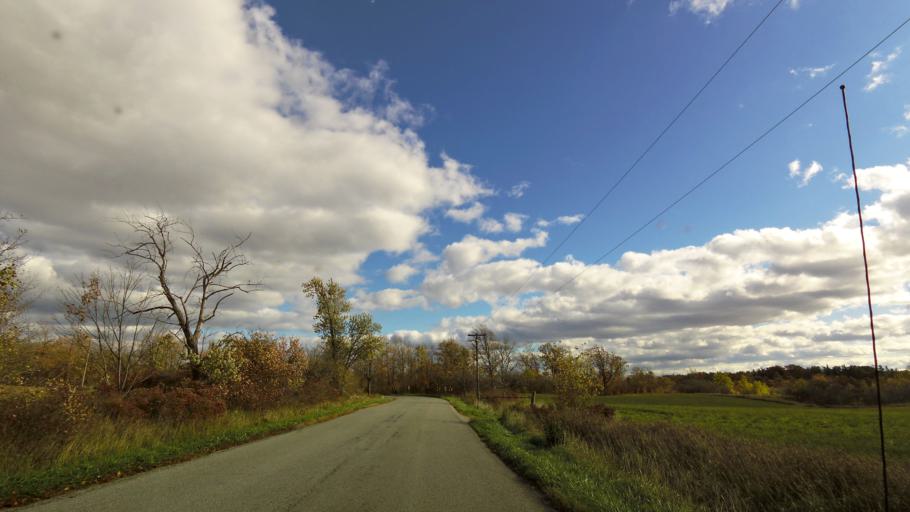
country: CA
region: Ontario
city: Burlington
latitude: 43.4409
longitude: -79.8432
